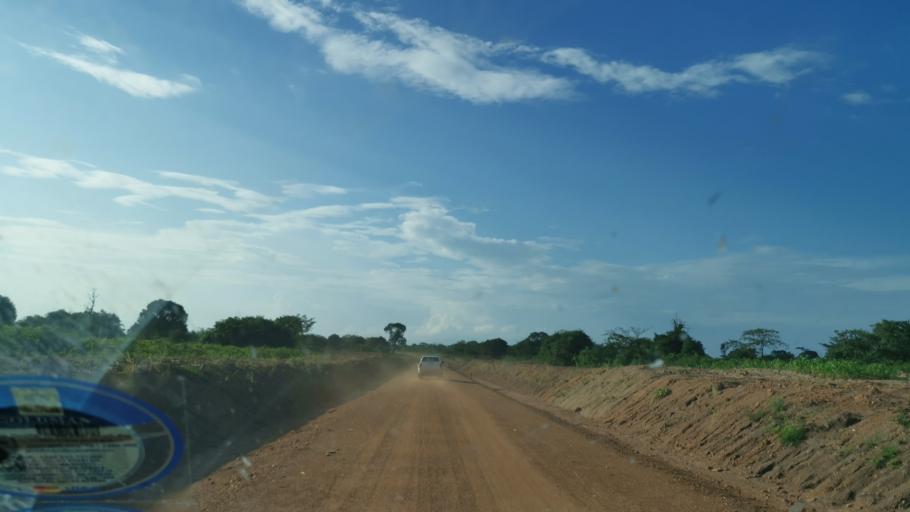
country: ZM
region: Luapula
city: Samfya
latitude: -11.1085
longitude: 29.5751
